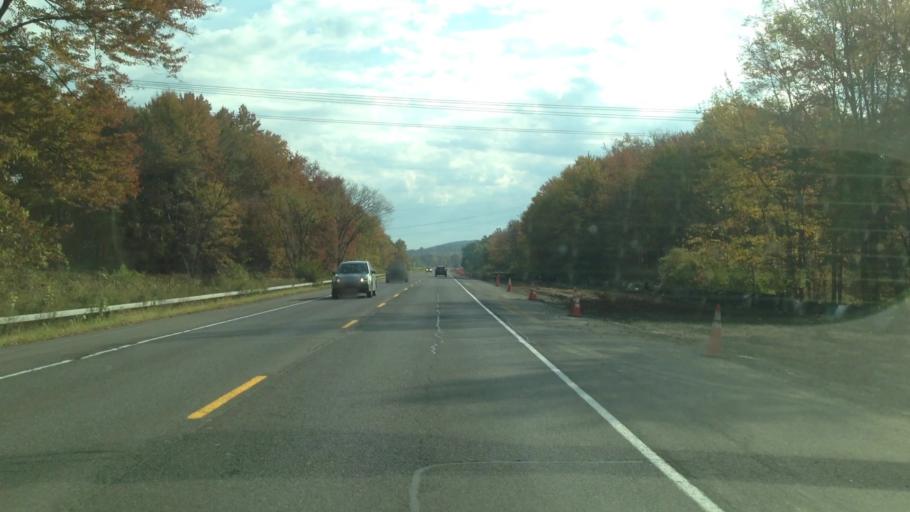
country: US
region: New York
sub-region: Ulster County
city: New Paltz
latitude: 41.7393
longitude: -74.0481
